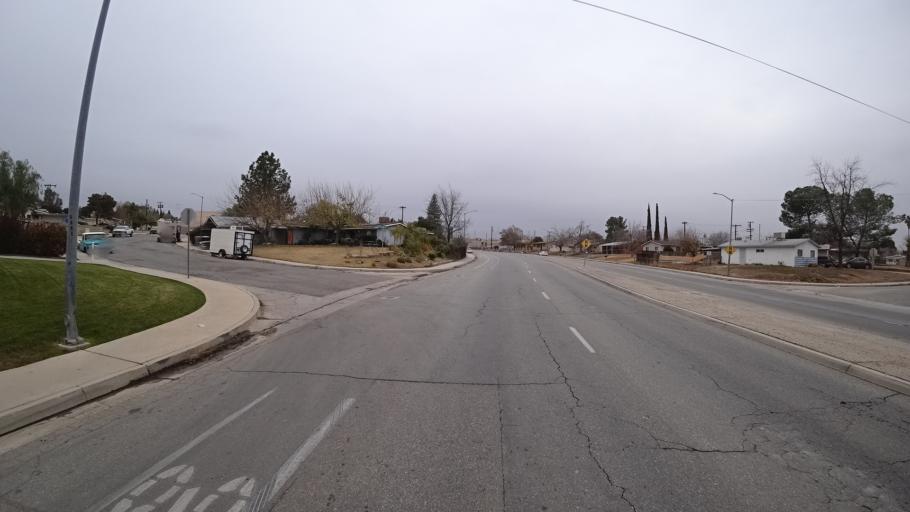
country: US
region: California
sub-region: Kern County
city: Bakersfield
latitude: 35.3819
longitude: -118.9314
